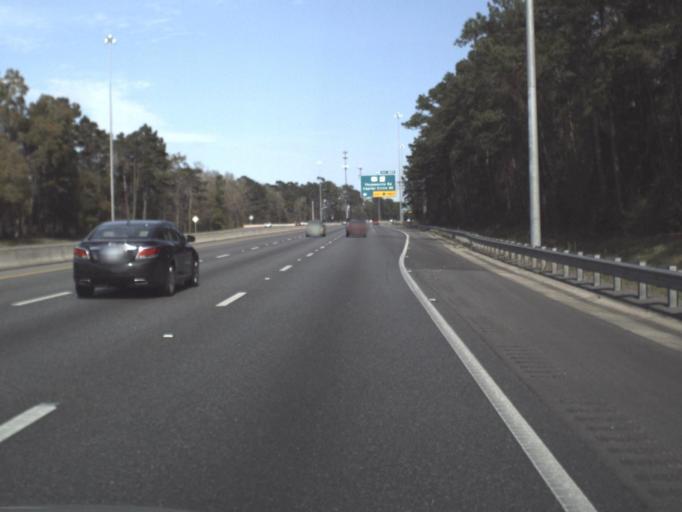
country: US
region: Florida
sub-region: Leon County
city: Tallahassee
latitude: 30.4980
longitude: -84.2660
